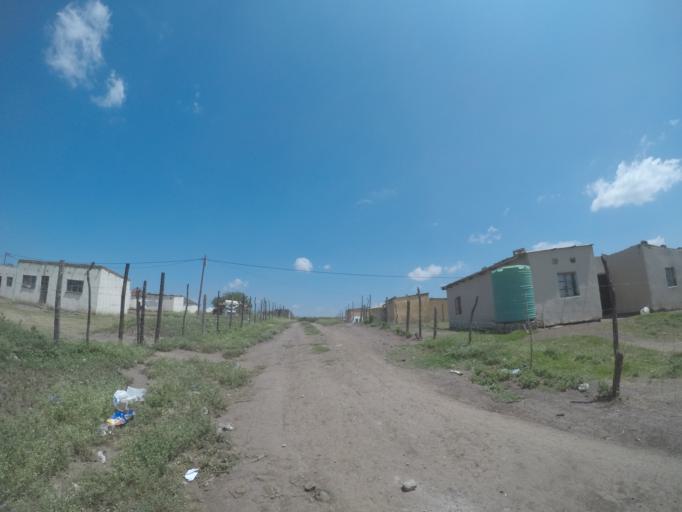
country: ZA
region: KwaZulu-Natal
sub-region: uThungulu District Municipality
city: Empangeni
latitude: -28.6085
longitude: 31.7384
